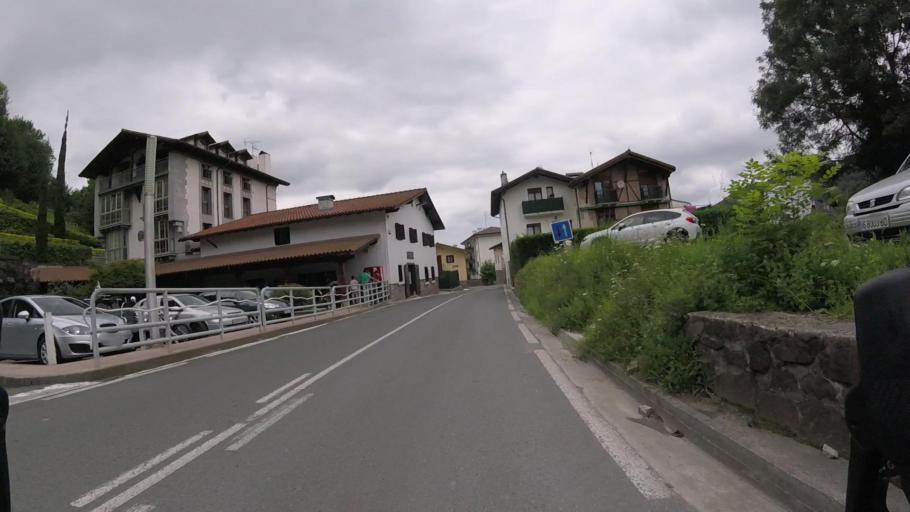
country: ES
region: Basque Country
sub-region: Provincia de Guipuzcoa
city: Lezo
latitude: 43.2878
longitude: -1.8366
